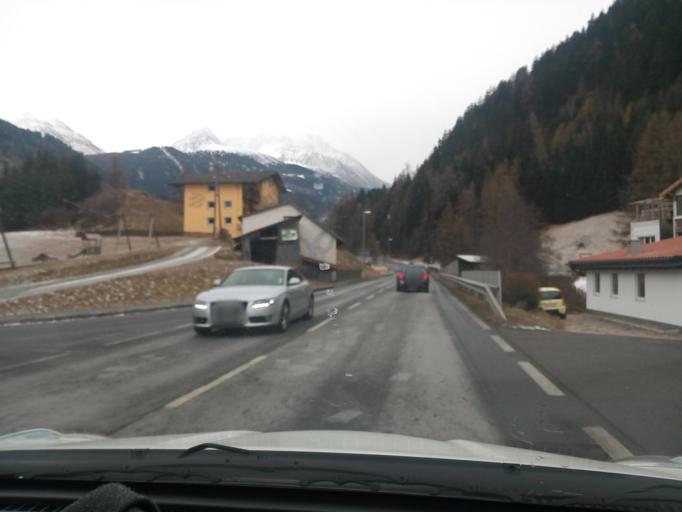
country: AT
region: Tyrol
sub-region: Politischer Bezirk Landeck
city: Nauders
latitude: 46.8878
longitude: 10.5007
